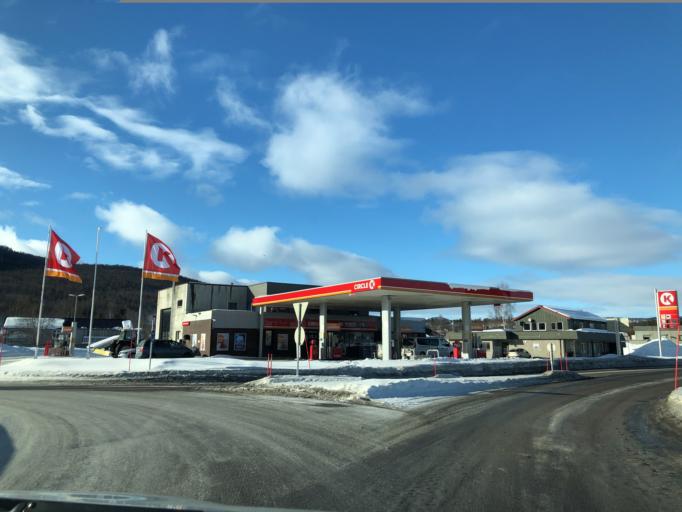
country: NO
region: Troms
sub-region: Malselv
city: Moen
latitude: 69.0438
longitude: 18.5108
